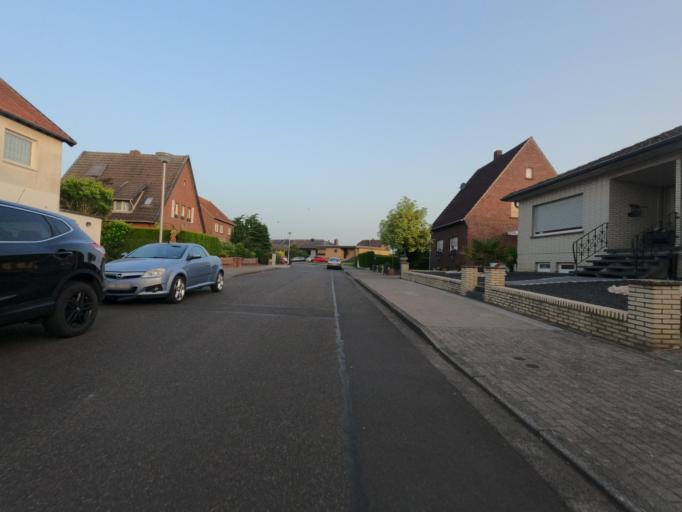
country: DE
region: North Rhine-Westphalia
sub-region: Regierungsbezirk Koln
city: Wassenberg
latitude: 51.0631
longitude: 6.1469
